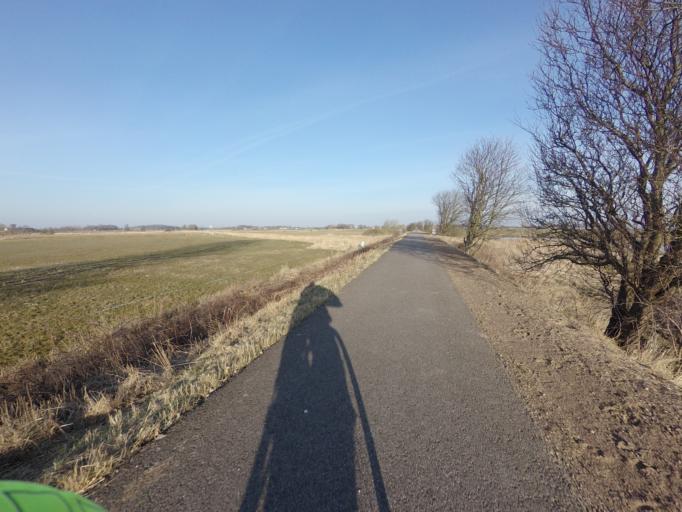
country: SE
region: Skane
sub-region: Hoganas Kommun
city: Hoganas
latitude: 56.1898
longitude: 12.6211
